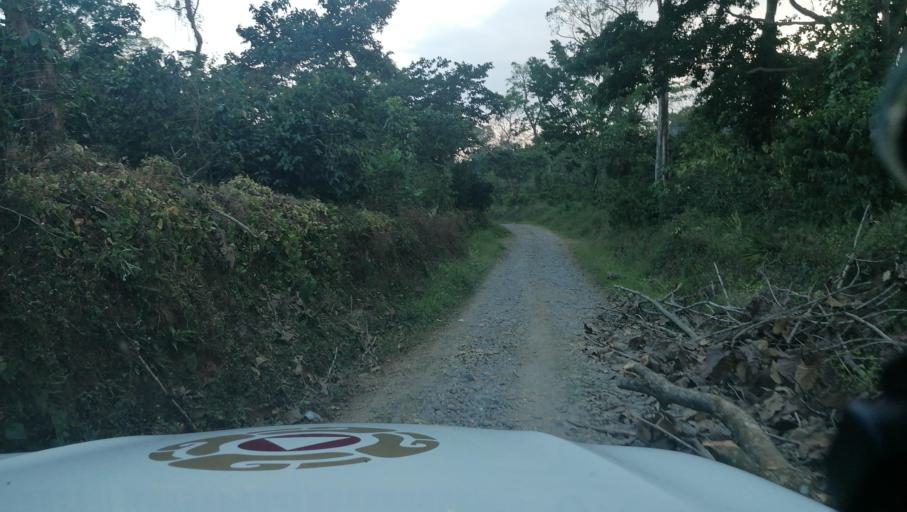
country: MX
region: Chiapas
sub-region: Cacahoatan
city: Benito Juarez
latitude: 15.0839
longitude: -92.2226
